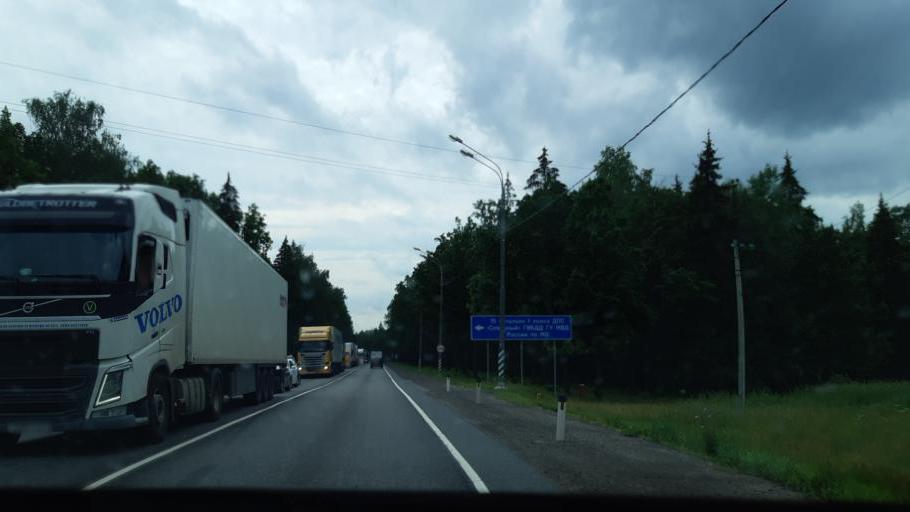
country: RU
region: Moskovskaya
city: Dorokhovo
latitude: 55.5272
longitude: 36.3563
